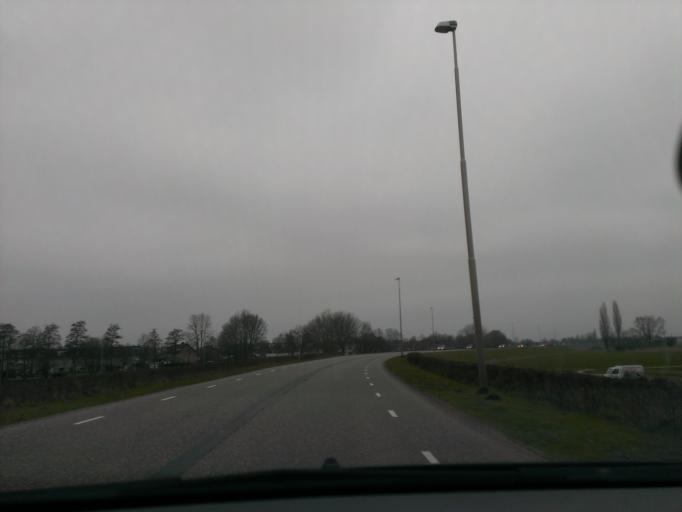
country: NL
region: Gelderland
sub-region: Gemeente Hattem
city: Hattem
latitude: 52.4777
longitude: 6.0664
